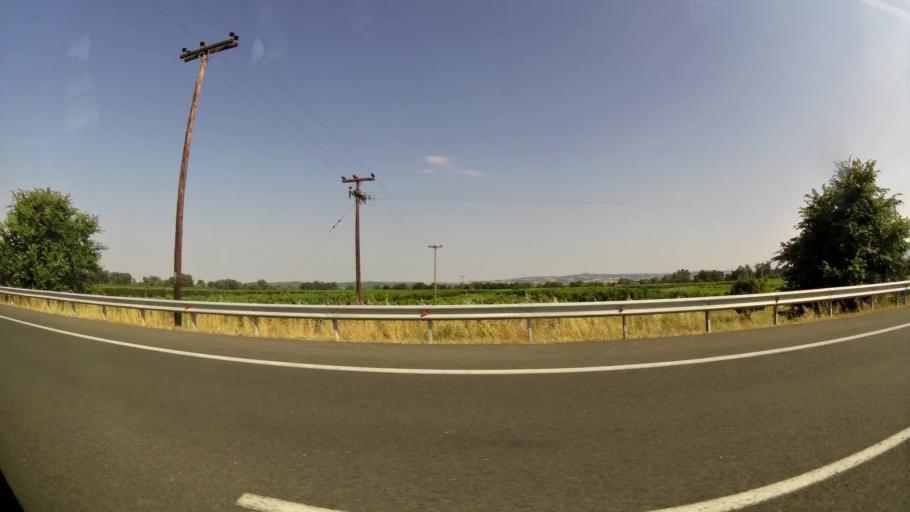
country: GR
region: Central Macedonia
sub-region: Nomos Imathias
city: Loutros
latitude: 40.5766
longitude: 22.4009
